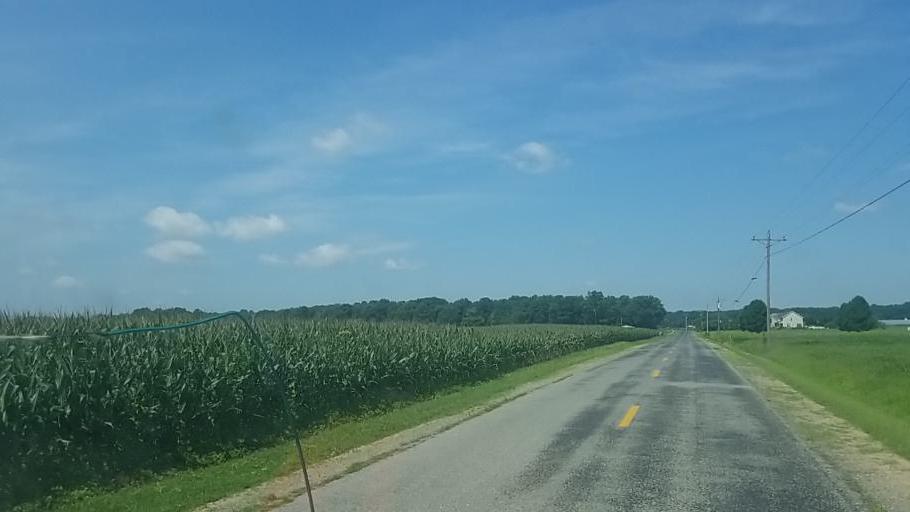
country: US
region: Maryland
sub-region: Caroline County
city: Denton
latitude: 38.8757
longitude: -75.7641
